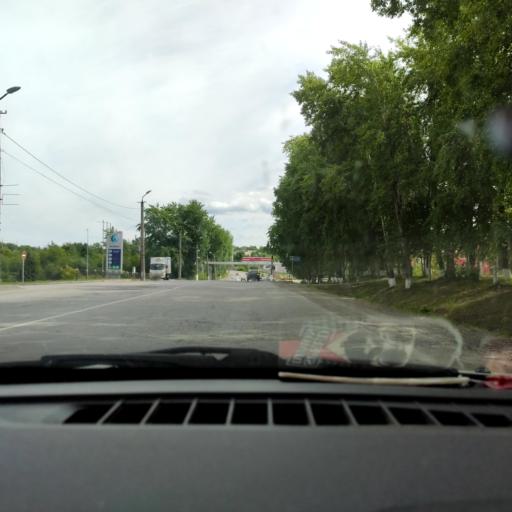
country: RU
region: Perm
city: Chusovoy
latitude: 58.2745
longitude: 57.8155
